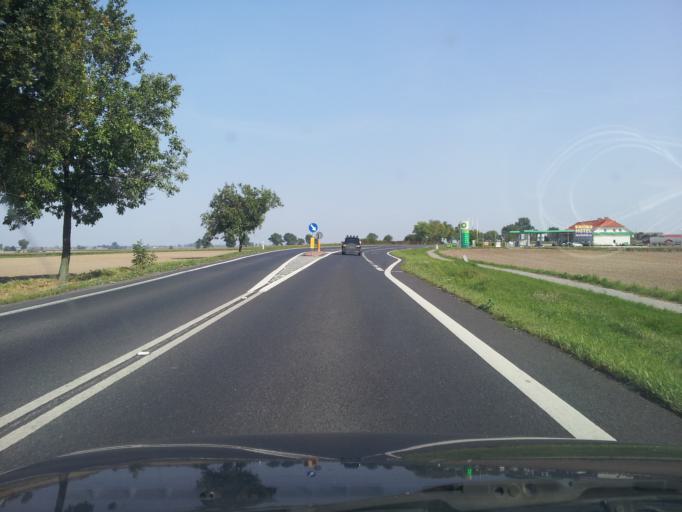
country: PL
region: Greater Poland Voivodeship
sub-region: Powiat gnieznienski
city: Lubowo
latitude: 52.5096
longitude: 17.3888
